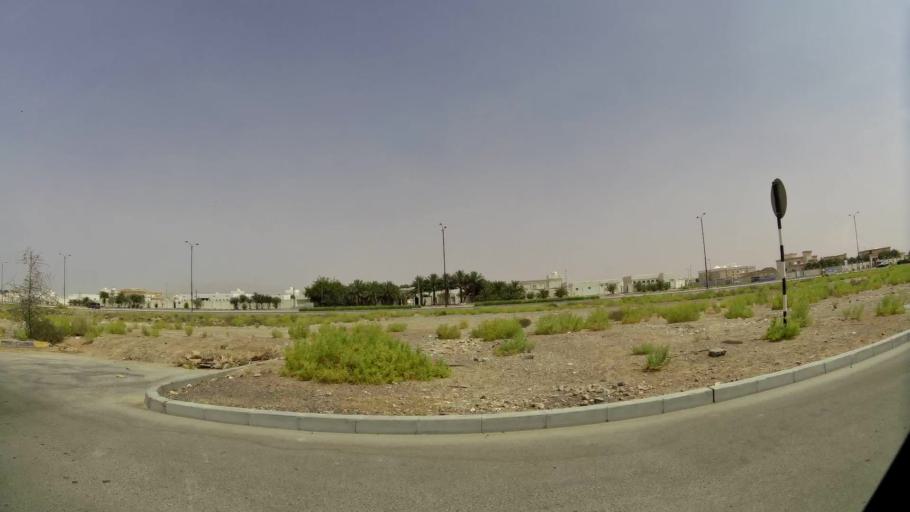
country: AE
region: Abu Dhabi
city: Al Ain
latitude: 24.1392
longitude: 55.6368
